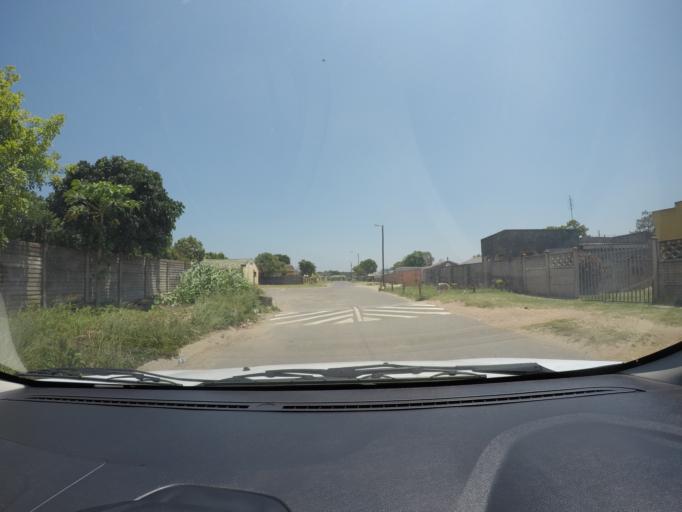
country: ZA
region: KwaZulu-Natal
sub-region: uThungulu District Municipality
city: eSikhawini
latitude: -28.8866
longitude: 31.8899
